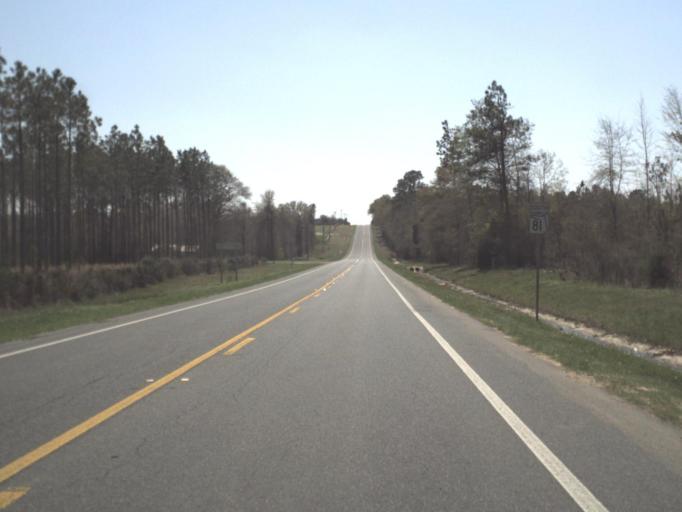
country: US
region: Alabama
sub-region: Geneva County
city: Geneva
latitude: 30.9318
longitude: -85.9663
